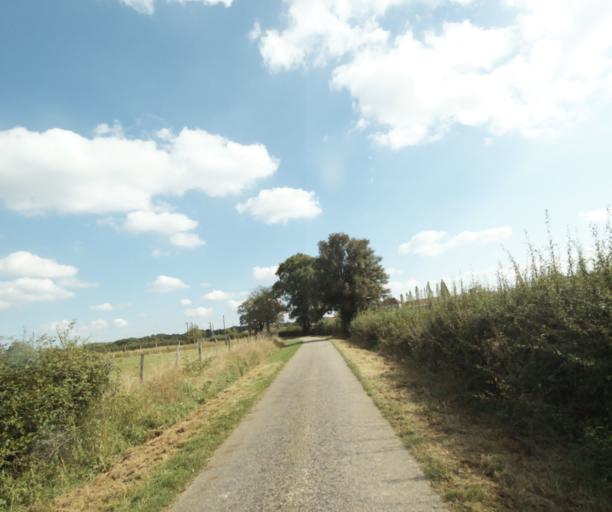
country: FR
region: Bourgogne
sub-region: Departement de Saone-et-Loire
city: Charolles
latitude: 46.4589
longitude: 4.2372
